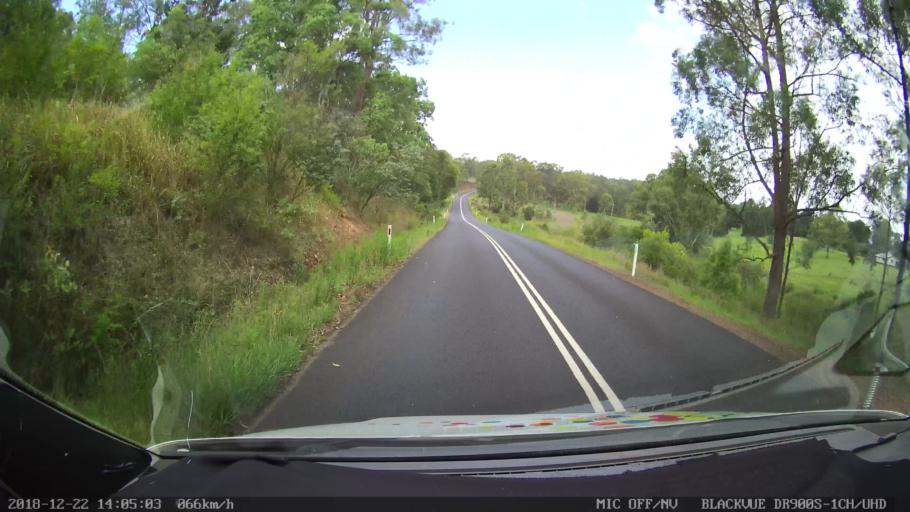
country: AU
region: New South Wales
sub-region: Clarence Valley
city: Coutts Crossing
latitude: -29.9409
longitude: 152.7271
